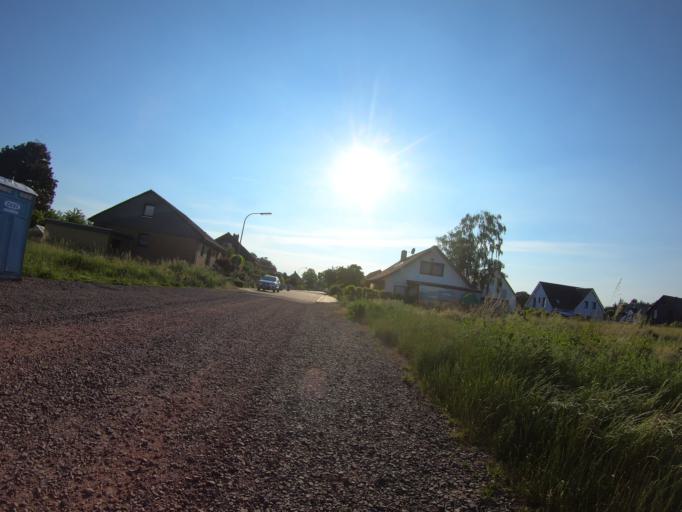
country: DE
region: Lower Saxony
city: Vordorf
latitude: 52.3651
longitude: 10.5262
